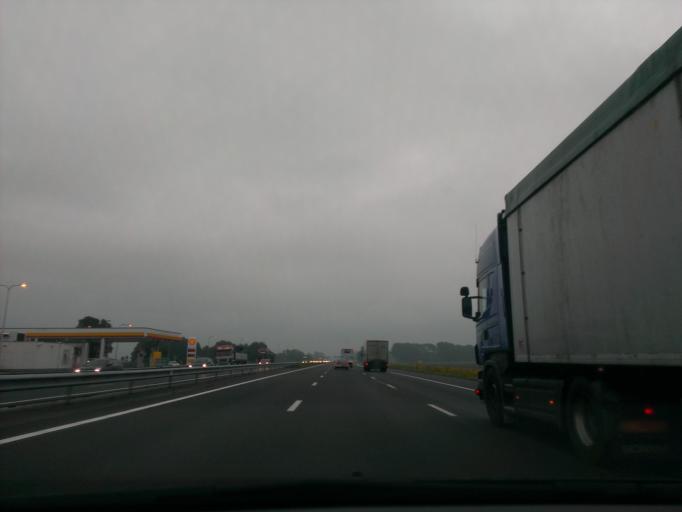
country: NL
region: Overijssel
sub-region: Gemeente Zwolle
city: Zwolle
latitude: 52.5453
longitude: 6.1684
